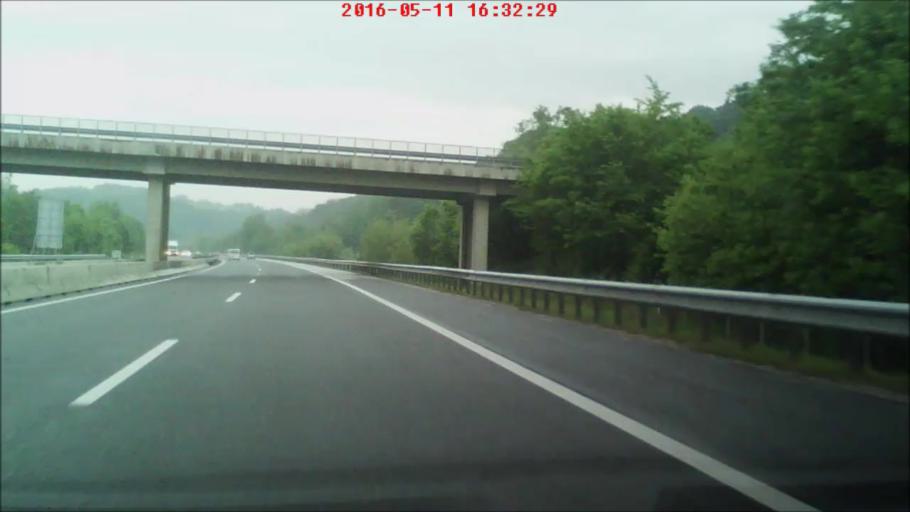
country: SI
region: Kungota
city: Zgornja Kungota
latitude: 46.6454
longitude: 15.6498
